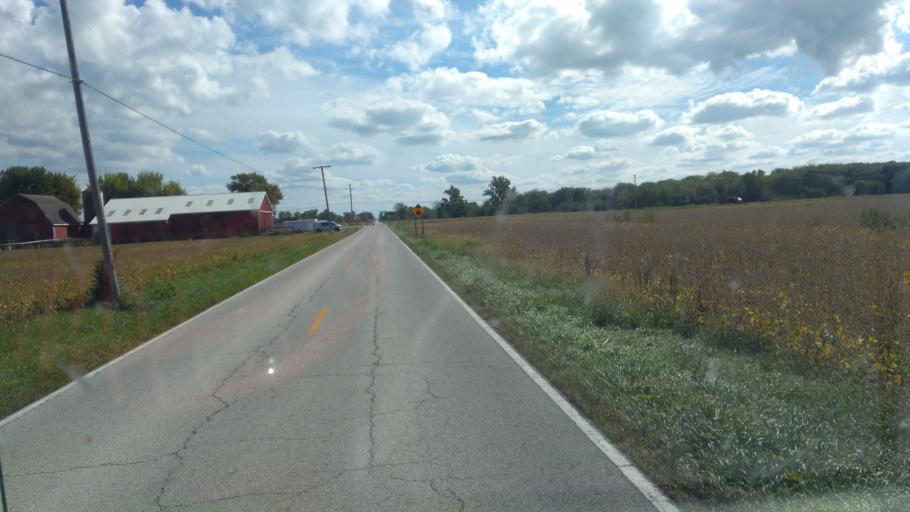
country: US
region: Ohio
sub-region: Sandusky County
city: Clyde
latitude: 41.3889
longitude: -82.9540
